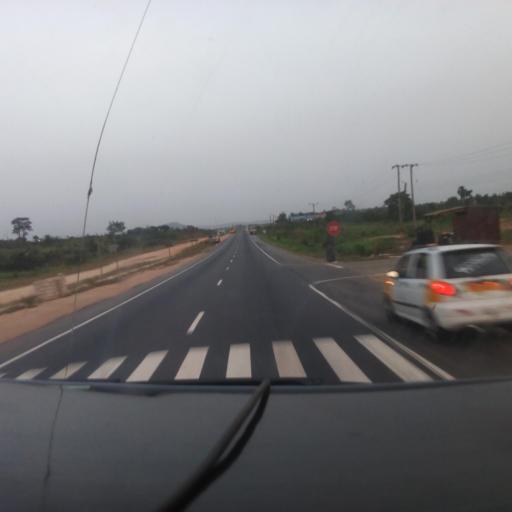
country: GH
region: Eastern
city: Nsawam
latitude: 5.8727
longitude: -0.3692
